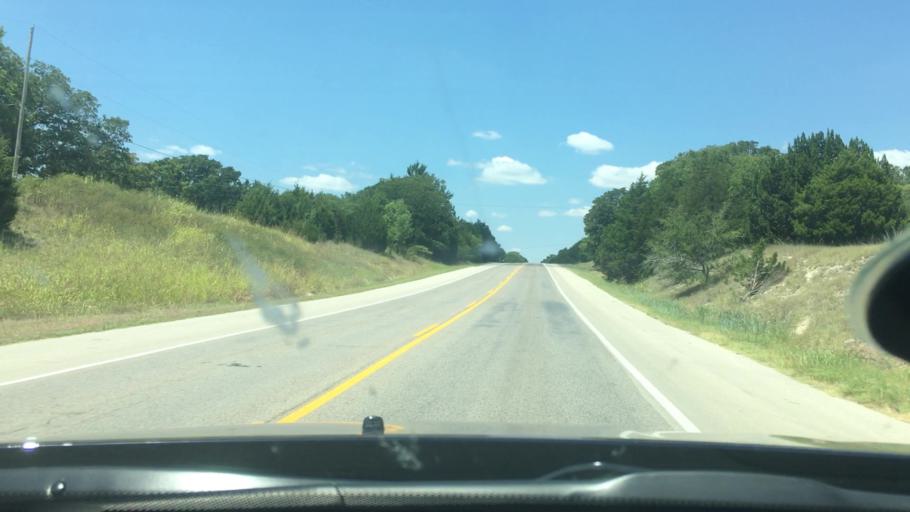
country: US
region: Oklahoma
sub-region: Carter County
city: Dickson
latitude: 34.1873
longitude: -96.9381
